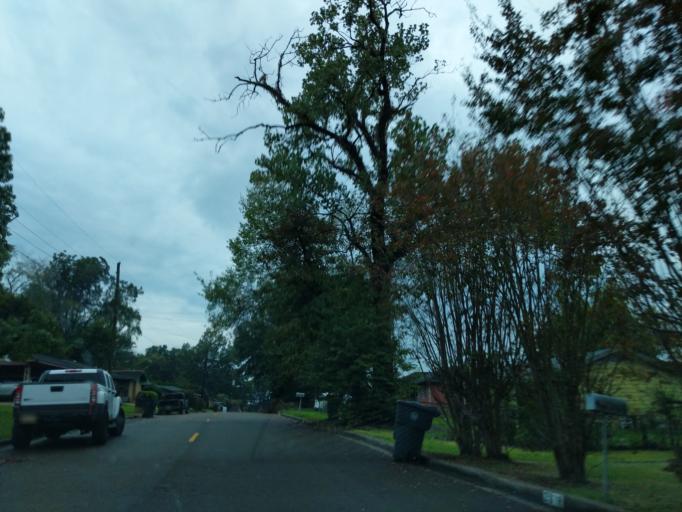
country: US
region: Mississippi
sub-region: Warren County
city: Vicksburg
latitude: 32.3363
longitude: -90.8898
